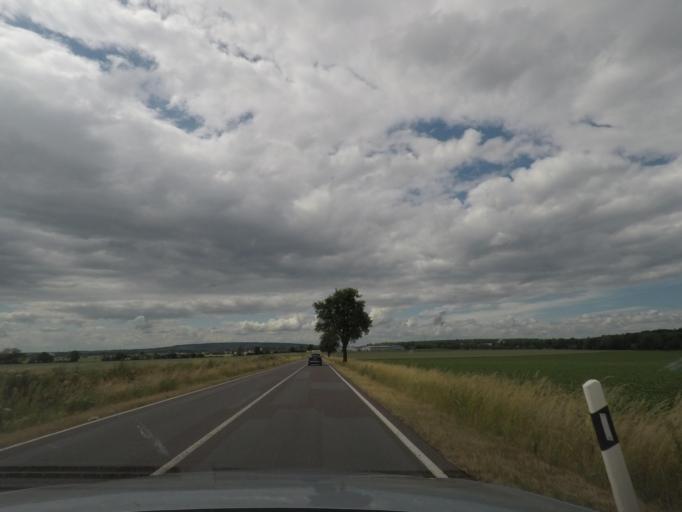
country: DE
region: Saxony-Anhalt
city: Hotensleben
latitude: 52.1077
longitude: 11.0375
